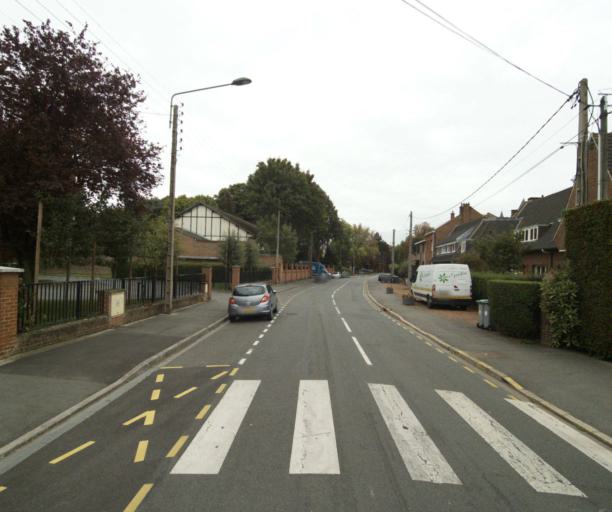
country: FR
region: Nord-Pas-de-Calais
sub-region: Departement du Nord
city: Lambersart
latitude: 50.6483
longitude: 3.0199
